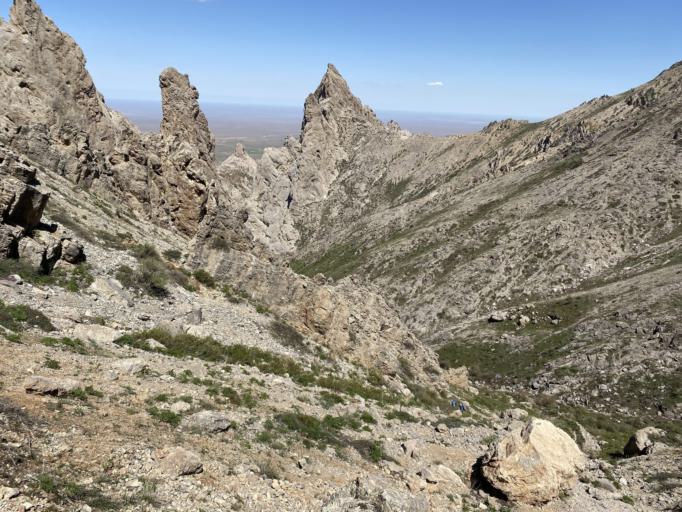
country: KZ
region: Ongtustik Qazaqstan
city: Ashchysay
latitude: 43.7634
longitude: 68.7880
